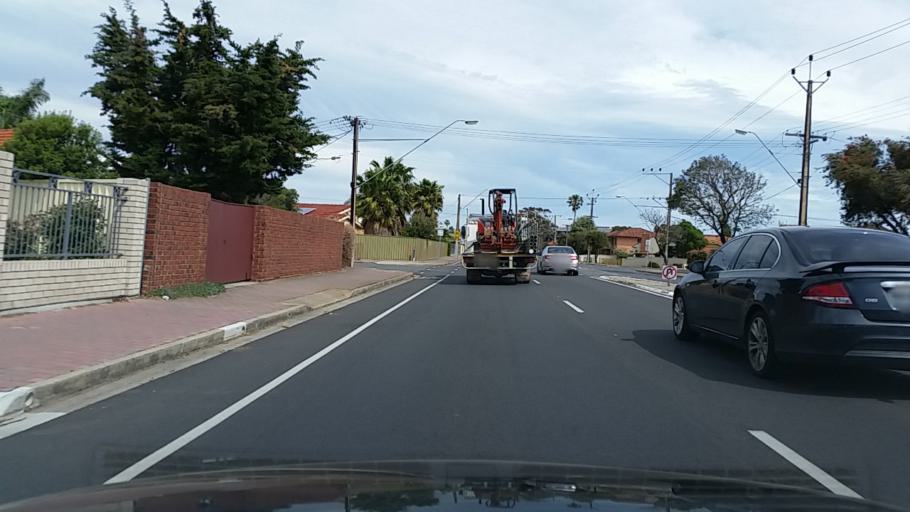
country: AU
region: South Australia
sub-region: Holdfast Bay
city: North Brighton
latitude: -34.9904
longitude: 138.5263
